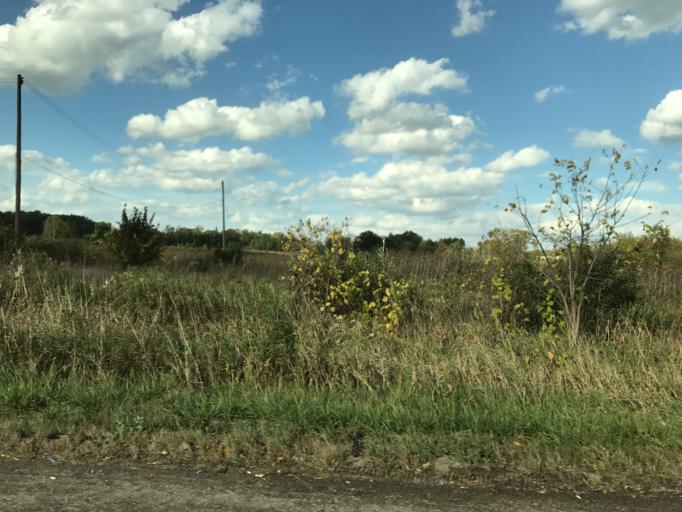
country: US
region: Michigan
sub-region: Oakland County
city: Wixom
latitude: 42.5061
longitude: -83.5895
